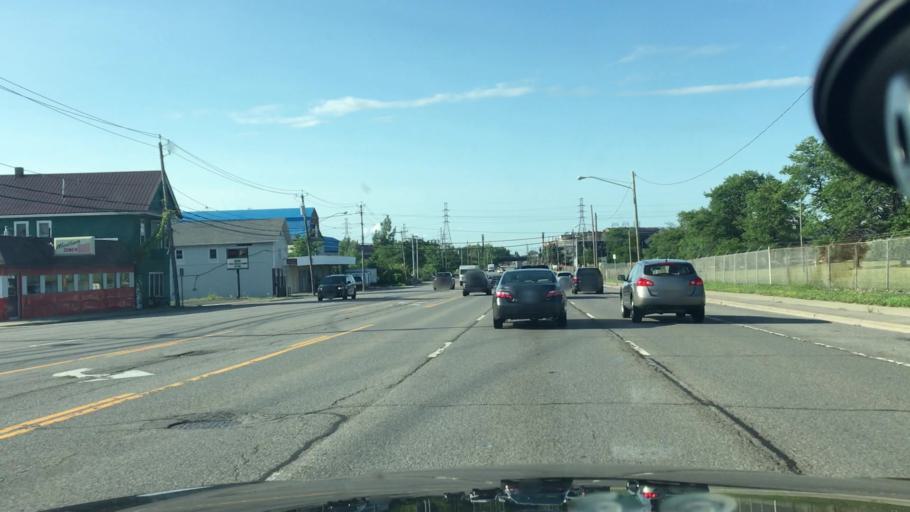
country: US
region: New York
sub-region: Erie County
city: Blasdell
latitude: 42.7987
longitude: -78.8467
